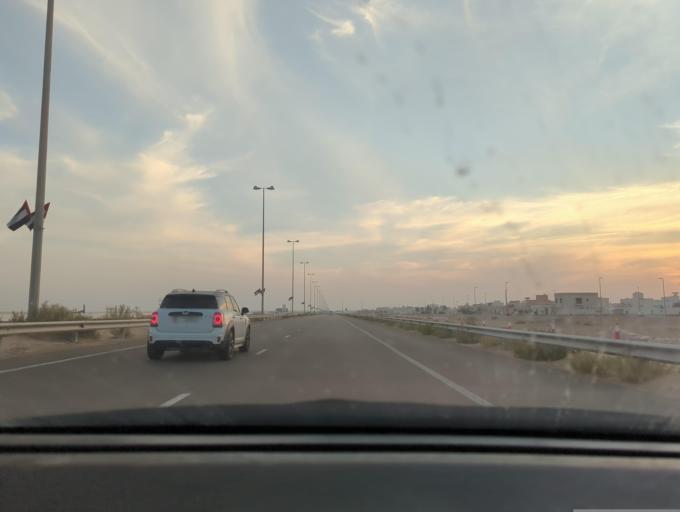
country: AE
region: Abu Dhabi
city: Abu Dhabi
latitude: 24.3531
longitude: 54.6626
